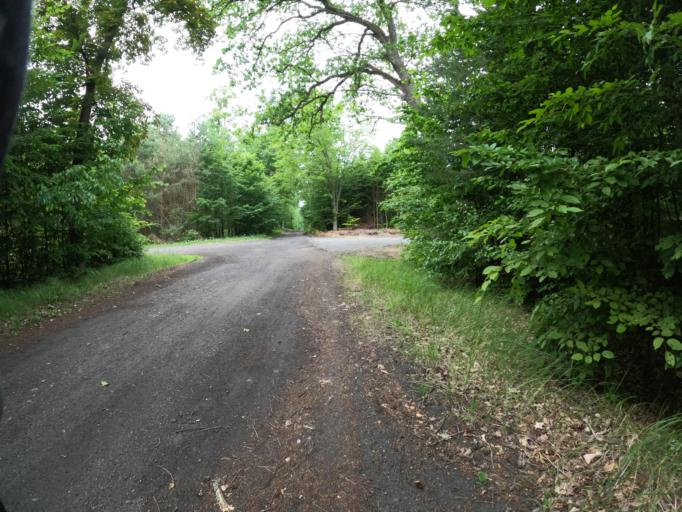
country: PL
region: West Pomeranian Voivodeship
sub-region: Powiat gryfinski
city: Mieszkowice
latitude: 52.7262
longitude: 14.4855
